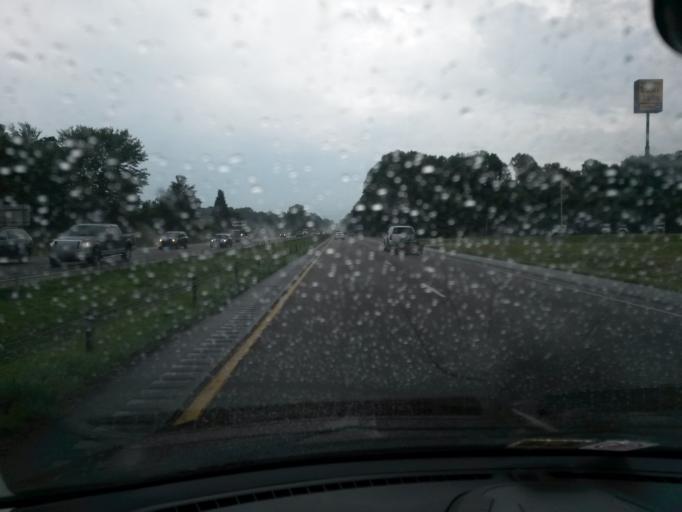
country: US
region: North Carolina
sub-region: Iredell County
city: Statesville
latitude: 35.7806
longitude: -80.9755
